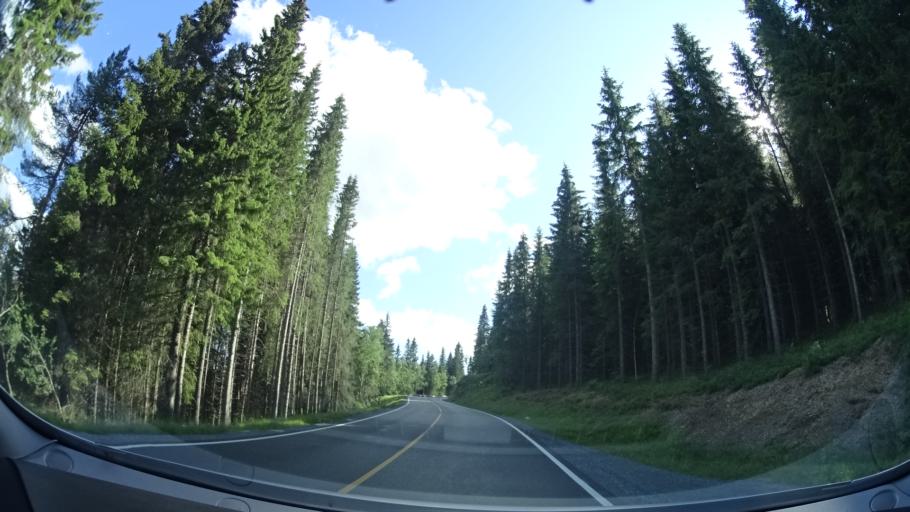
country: NO
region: Sor-Trondelag
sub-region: Snillfjord
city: Krokstadora
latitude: 63.2322
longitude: 9.5781
